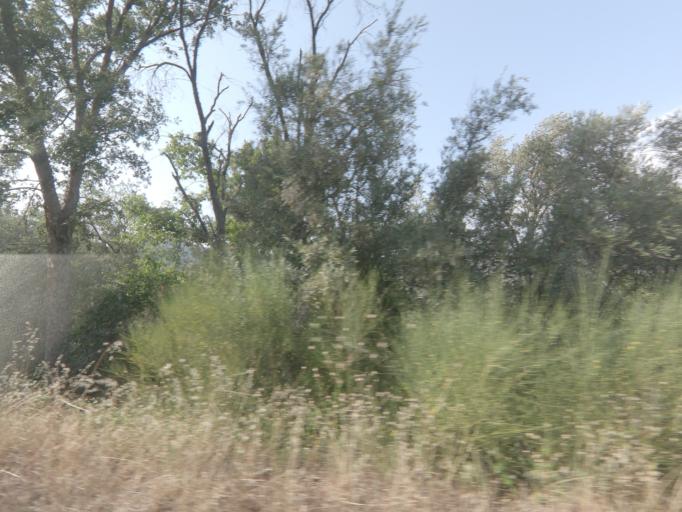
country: PT
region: Viseu
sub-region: Tabuaco
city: Tabuaco
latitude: 41.1217
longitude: -7.5496
